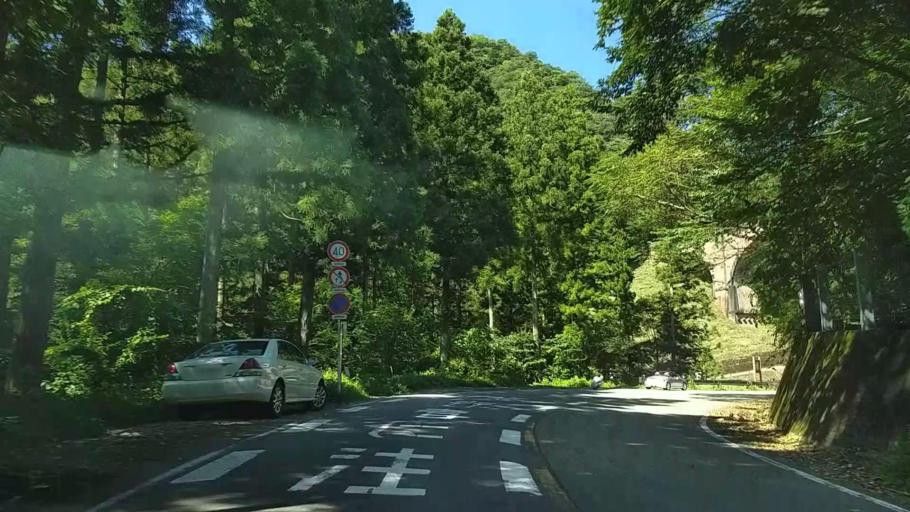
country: JP
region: Gunma
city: Annaka
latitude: 36.3575
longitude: 138.6994
